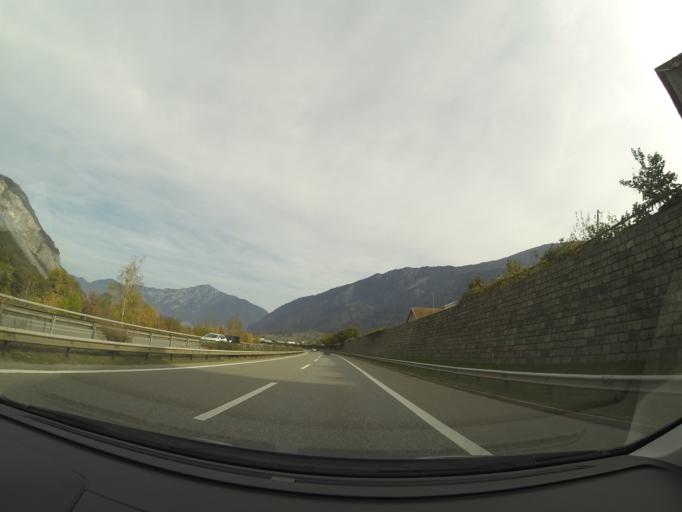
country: CH
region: Grisons
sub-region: Imboden District
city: Domat
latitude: 46.8386
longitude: 9.4567
